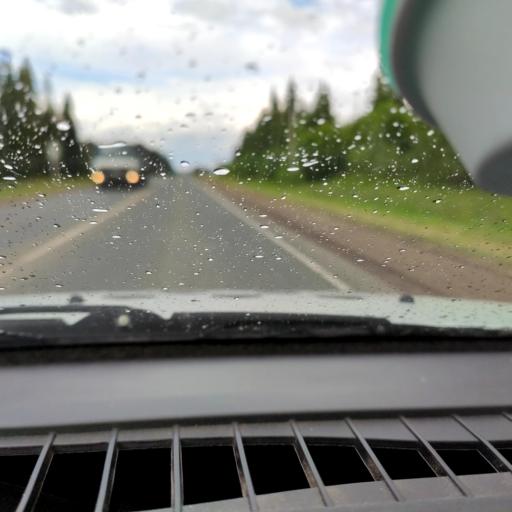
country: RU
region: Perm
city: Orda
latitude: 57.2015
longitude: 56.9200
